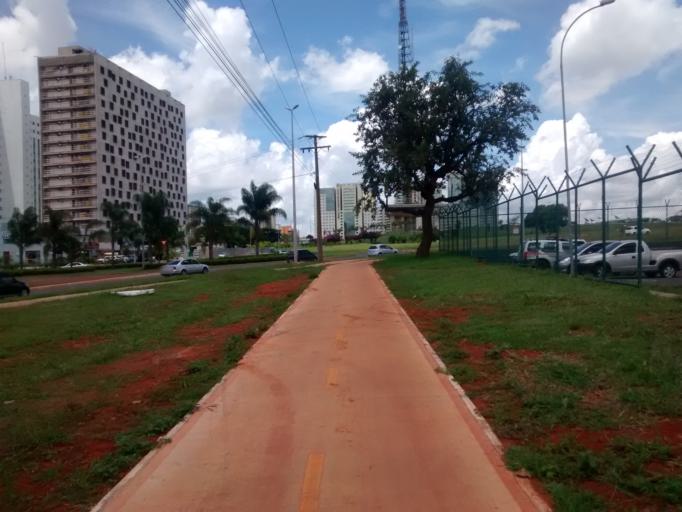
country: BR
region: Federal District
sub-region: Brasilia
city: Brasilia
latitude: -15.7868
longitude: -47.8917
